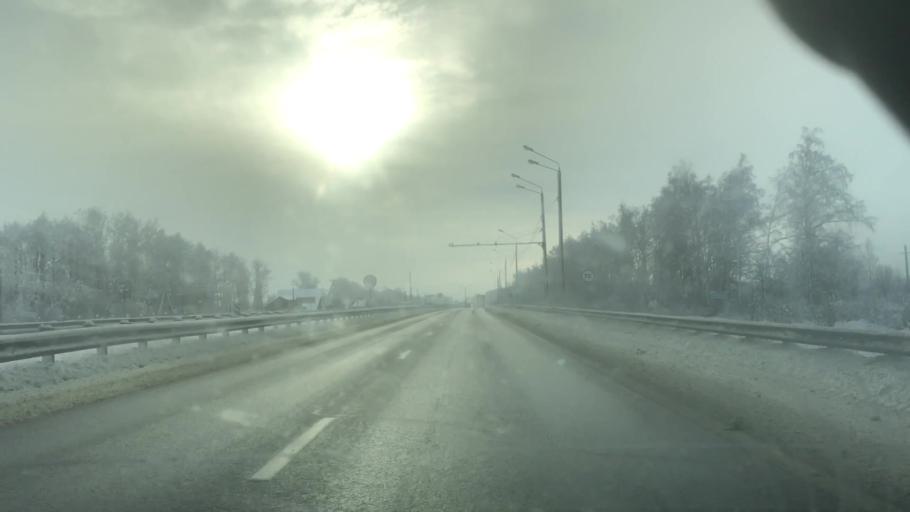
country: RU
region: Tula
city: Venev
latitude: 54.3470
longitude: 38.1540
